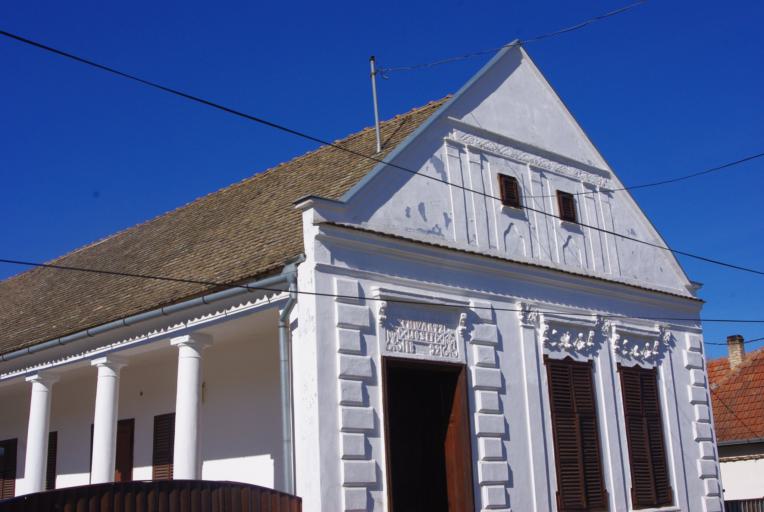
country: HU
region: Tolna
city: Bataszek
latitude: 46.1850
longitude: 18.7260
